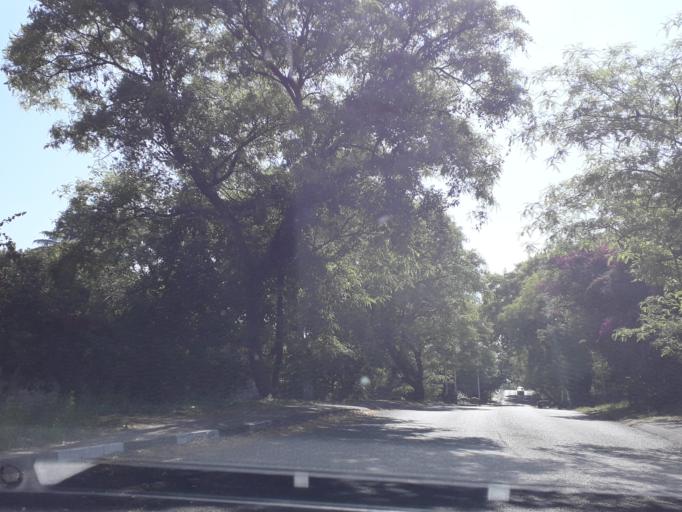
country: ZA
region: Gauteng
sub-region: City of Johannesburg Metropolitan Municipality
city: Johannesburg
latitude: -26.1247
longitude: 27.9835
